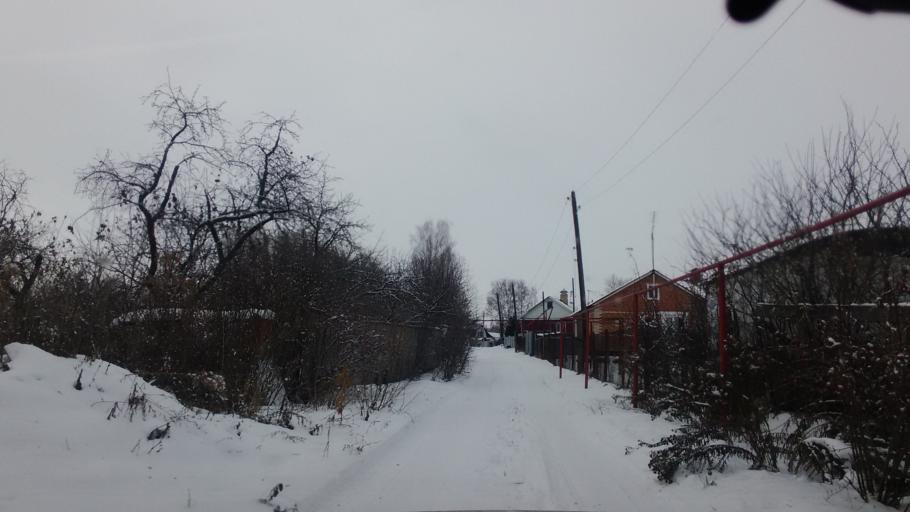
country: RU
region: Tula
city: Bogoroditsk
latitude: 53.7580
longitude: 38.1221
